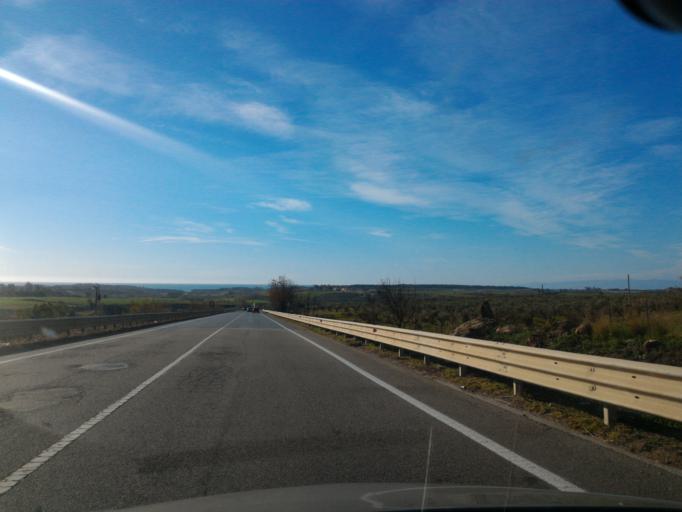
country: IT
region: Calabria
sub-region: Provincia di Crotone
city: Isola di Capo Rizzuto
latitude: 38.9452
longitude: 17.0815
